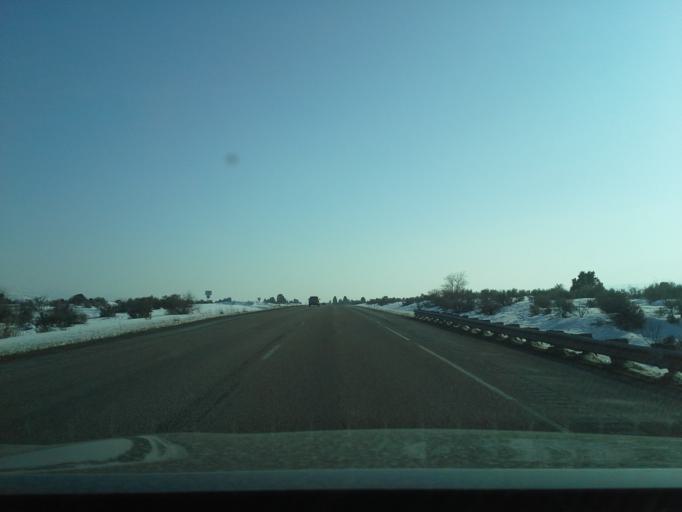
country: US
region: Idaho
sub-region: Bannock County
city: Pocatello
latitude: 42.7733
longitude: -112.2297
